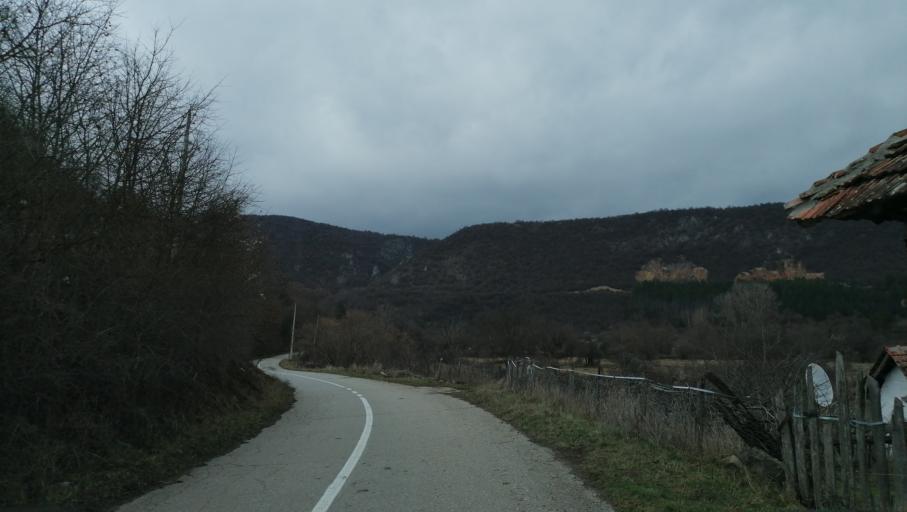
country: RS
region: Central Serbia
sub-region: Pirotski Okrug
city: Dimitrovgrad
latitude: 42.9295
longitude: 22.7723
